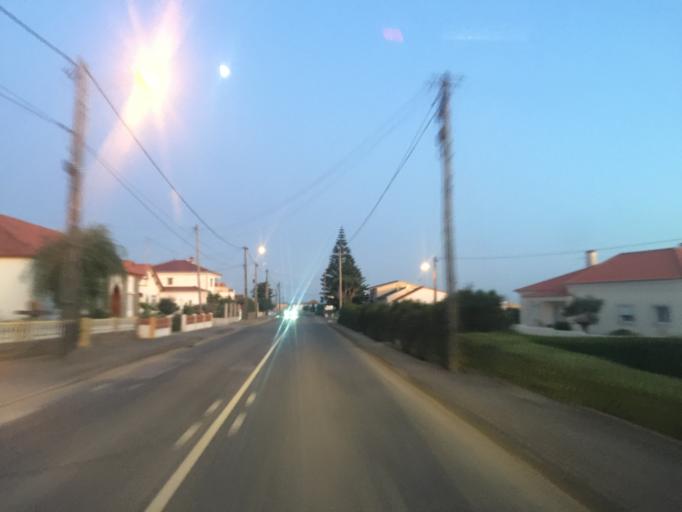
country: PT
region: Lisbon
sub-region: Lourinha
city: Lourinha
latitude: 39.2817
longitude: -9.3015
